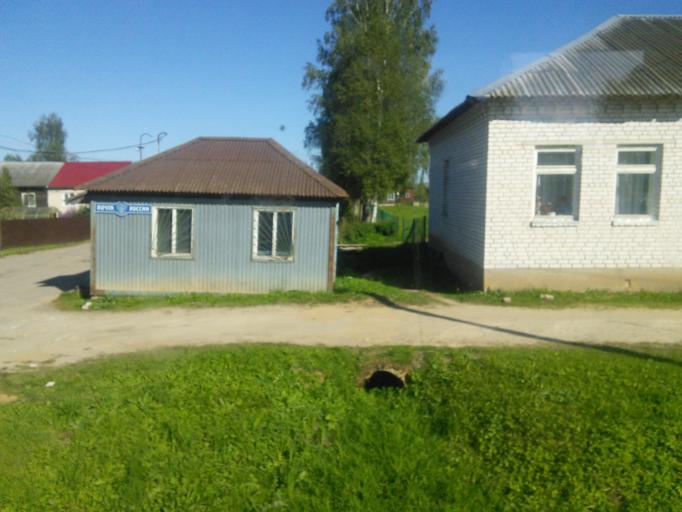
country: RU
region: Tverskaya
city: Kesova Gora
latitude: 57.5902
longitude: 37.2916
